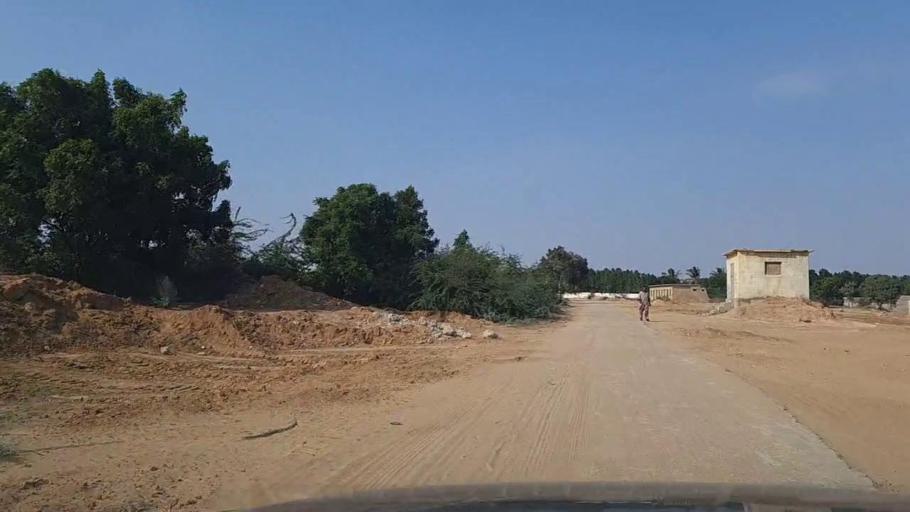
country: PK
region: Sindh
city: Gharo
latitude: 24.7663
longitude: 67.5771
